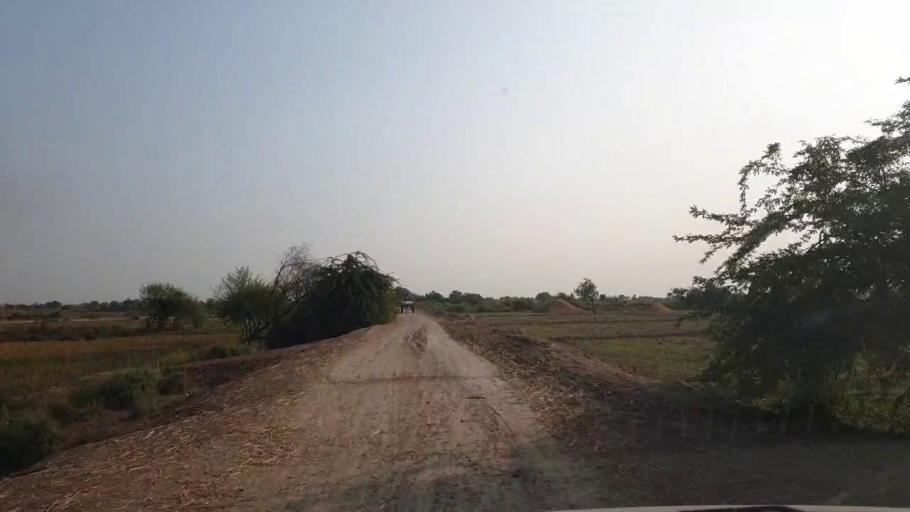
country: PK
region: Sindh
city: Rajo Khanani
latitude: 25.0288
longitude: 68.7785
